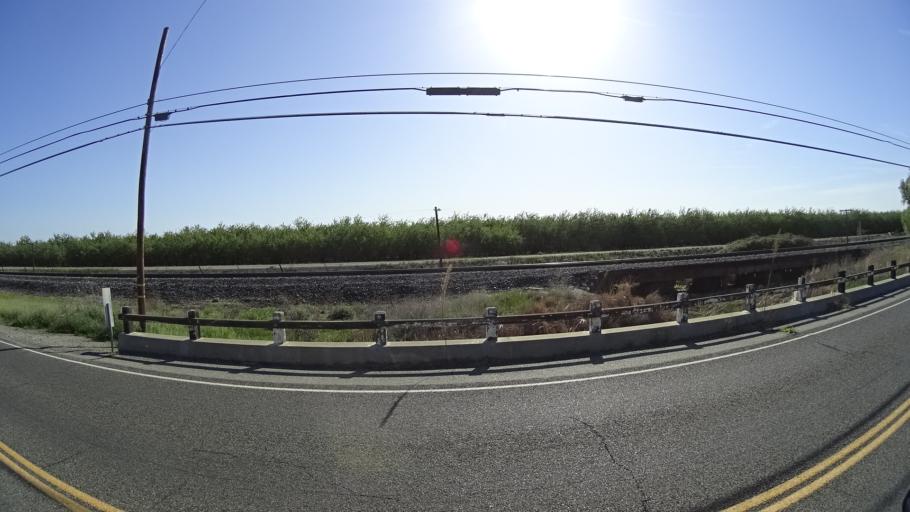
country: US
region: California
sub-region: Glenn County
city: Willows
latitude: 39.5708
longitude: -122.1939
